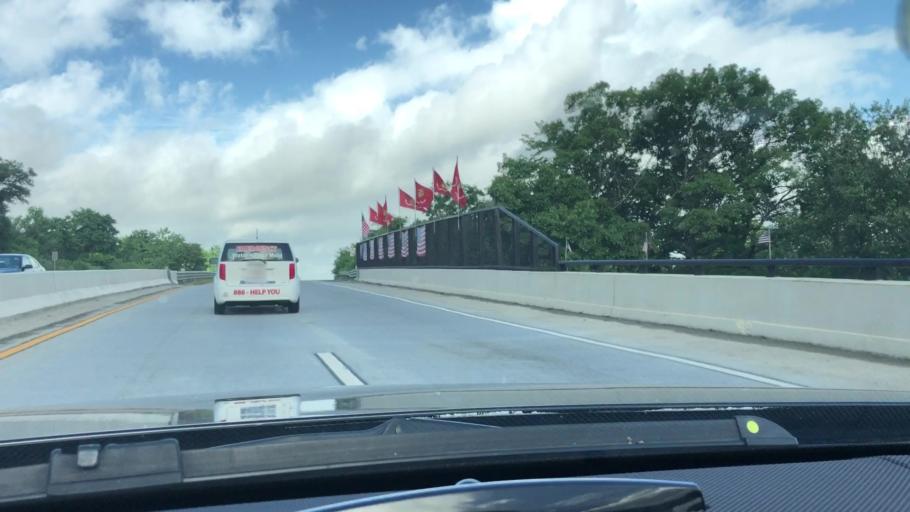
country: US
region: Massachusetts
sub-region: Norfolk County
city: Franklin
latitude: 42.0891
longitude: -71.4326
